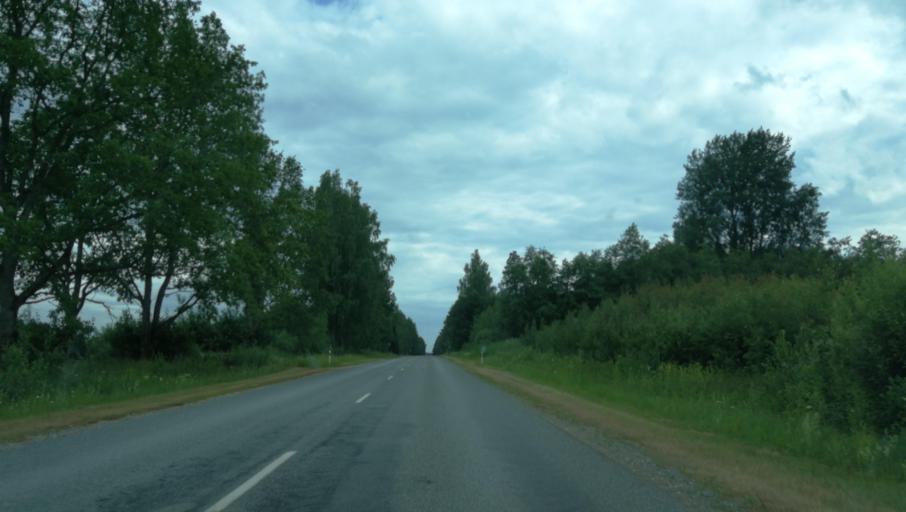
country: LV
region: Valmieras Rajons
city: Valmiera
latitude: 57.7067
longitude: 25.4262
